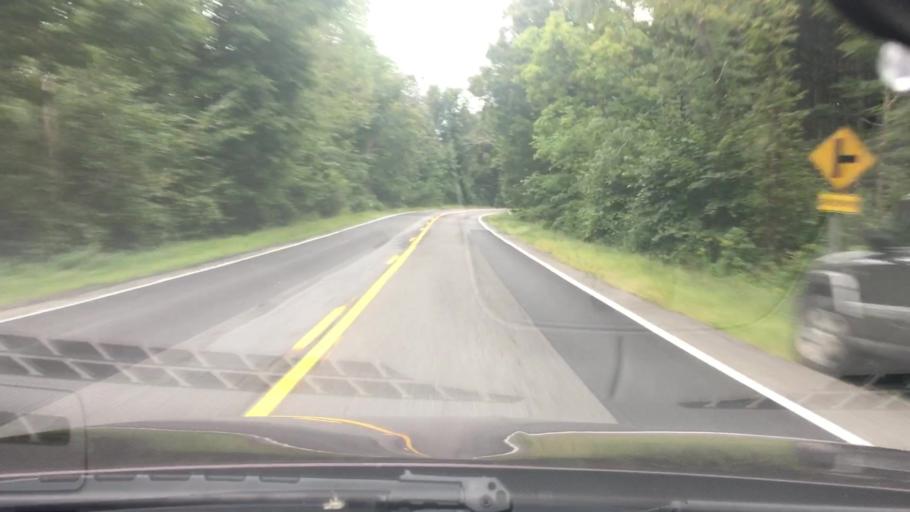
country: US
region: New York
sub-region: Dutchess County
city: Millbrook
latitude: 41.7939
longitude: -73.7080
